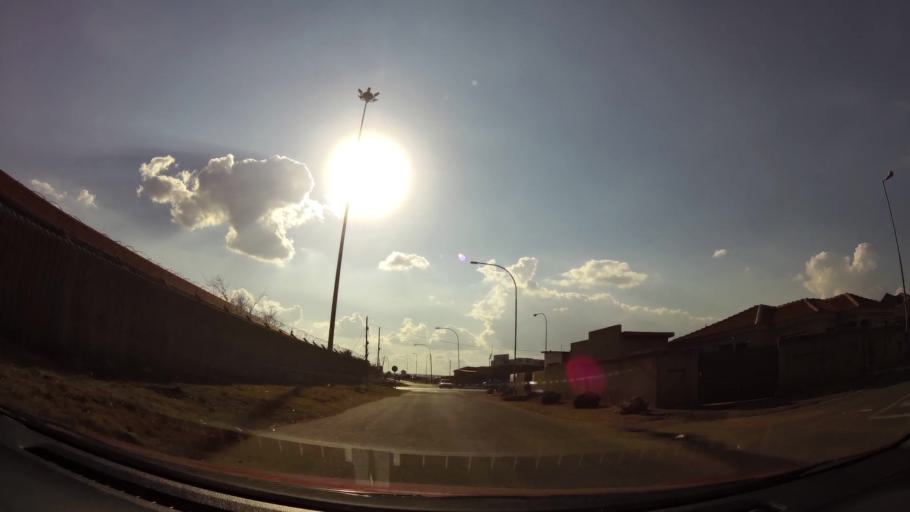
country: ZA
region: Gauteng
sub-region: City of Johannesburg Metropolitan Municipality
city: Soweto
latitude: -26.2327
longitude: 27.8664
